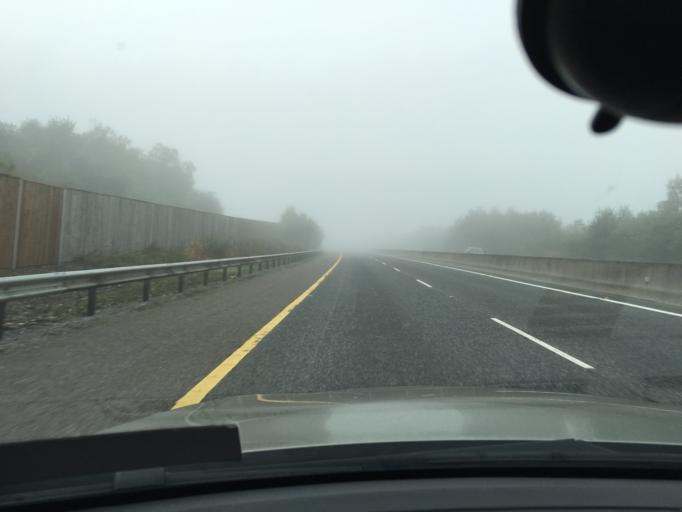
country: IE
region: Leinster
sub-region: An Iarmhi
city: Kilbeggan
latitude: 53.3701
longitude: -7.3959
